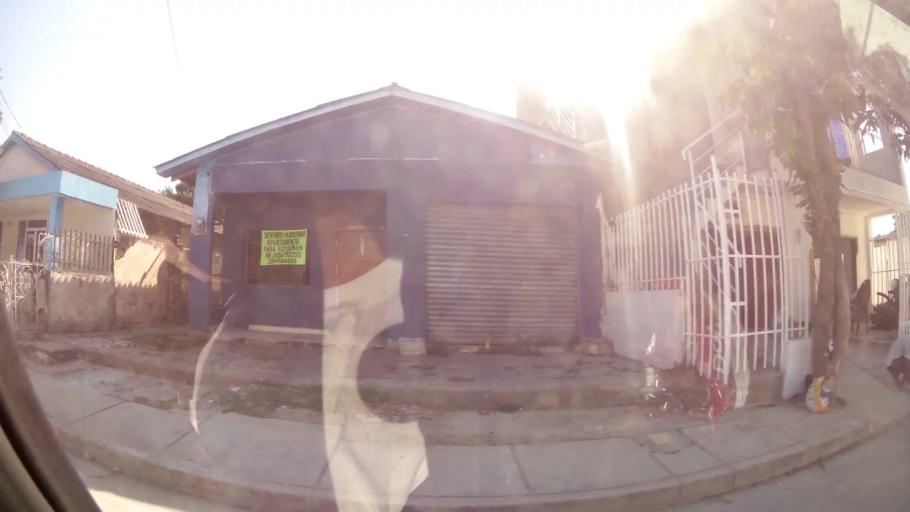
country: CO
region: Bolivar
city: Cartagena
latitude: 10.4025
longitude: -75.4970
